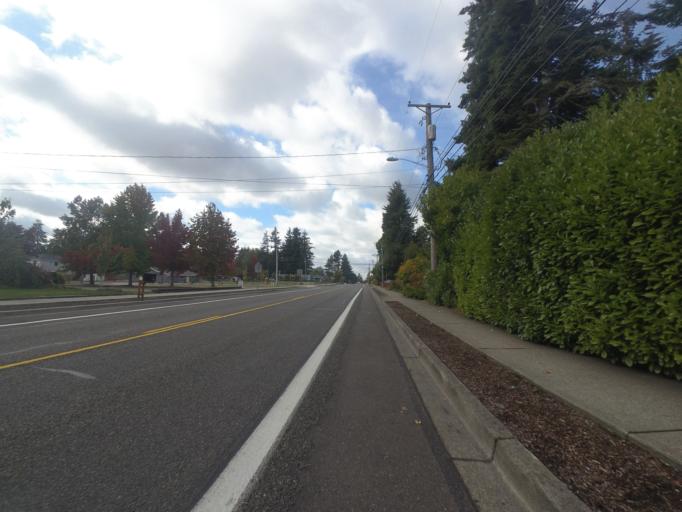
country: US
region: Washington
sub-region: Pierce County
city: University Place
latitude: 47.2172
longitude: -122.5431
